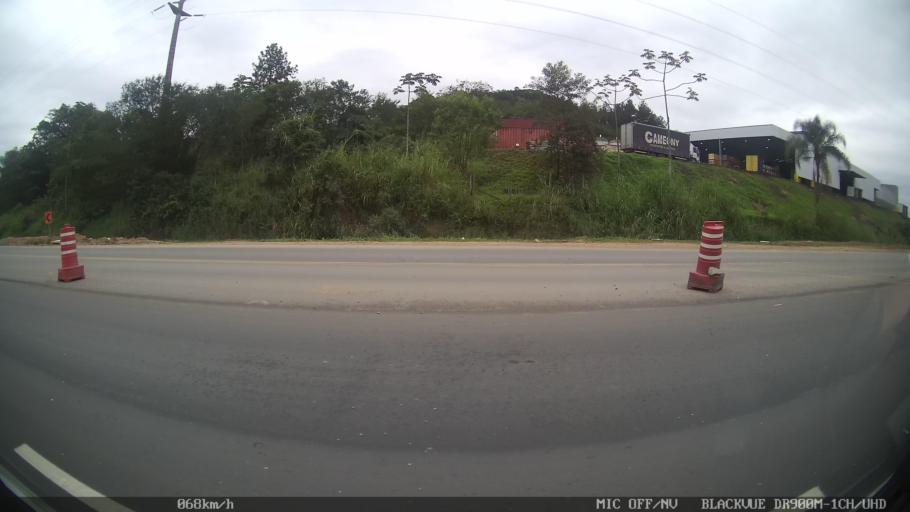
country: BR
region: Santa Catarina
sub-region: Joinville
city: Joinville
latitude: -26.2567
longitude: -48.8793
